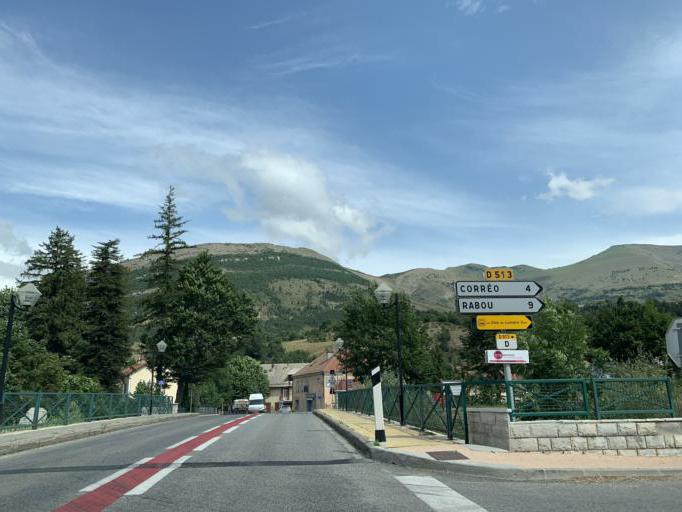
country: FR
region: Provence-Alpes-Cote d'Azur
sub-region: Departement des Hautes-Alpes
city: La Roche-des-Arnauds
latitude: 44.5609
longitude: 5.9563
